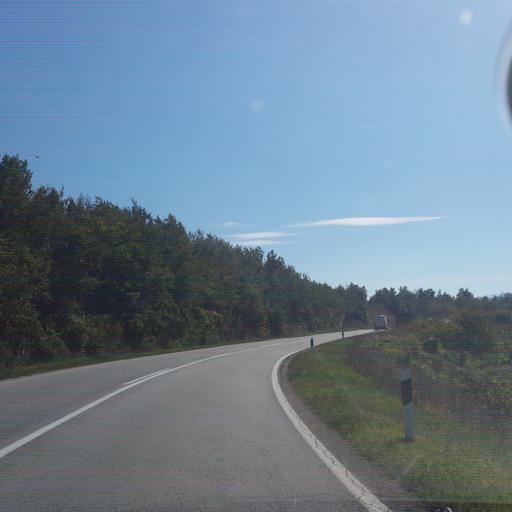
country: RS
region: Central Serbia
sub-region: Zajecarski Okrug
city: Knjazevac
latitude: 43.4806
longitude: 22.2311
